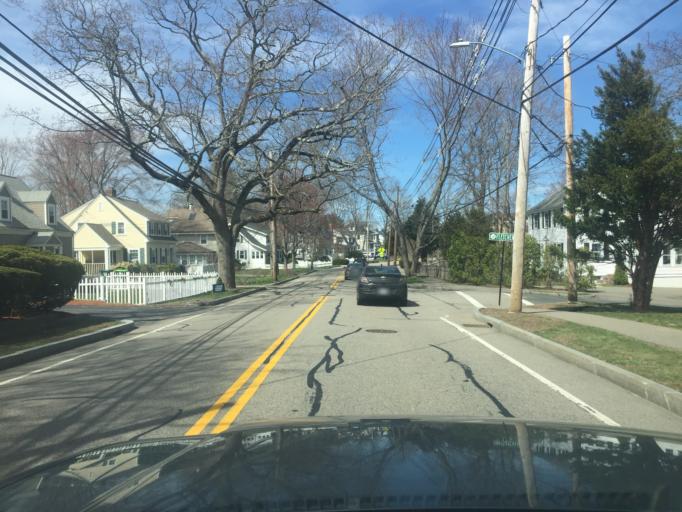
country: US
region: Massachusetts
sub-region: Norfolk County
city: Needham
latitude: 42.2684
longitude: -71.2384
